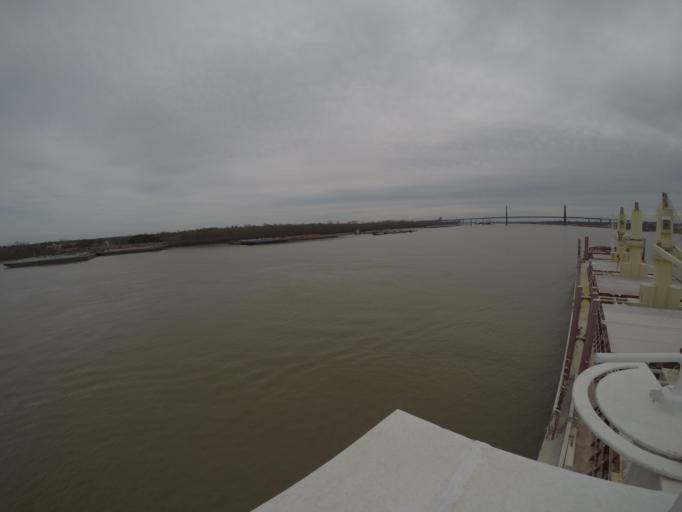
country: US
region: Louisiana
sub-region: Saint Charles Parish
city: New Sarpy
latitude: 29.9511
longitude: -90.3923
